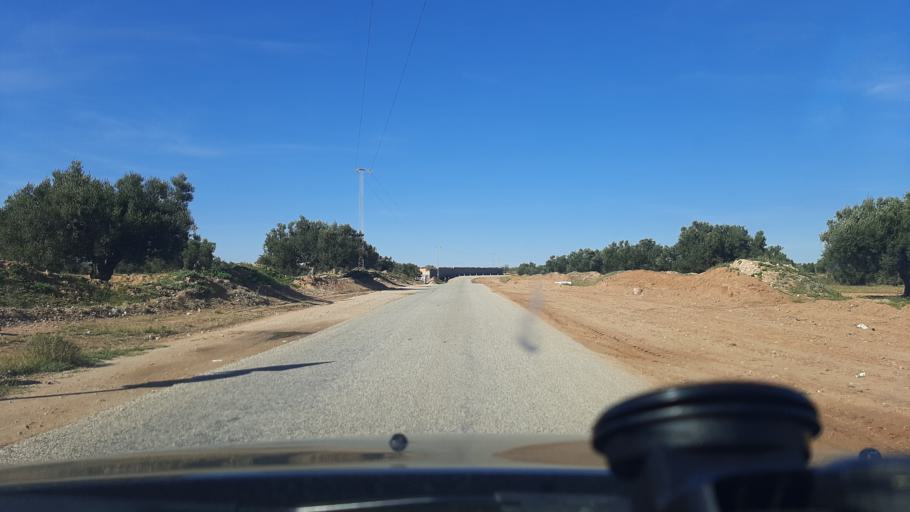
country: TN
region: Safaqis
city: Sfax
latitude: 34.9098
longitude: 10.5913
